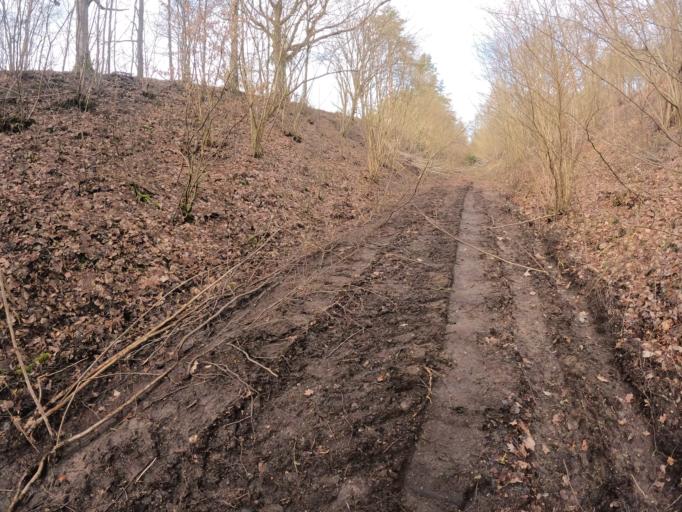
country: PL
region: West Pomeranian Voivodeship
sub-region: Powiat koszalinski
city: Bobolice
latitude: 53.9727
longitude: 16.5718
